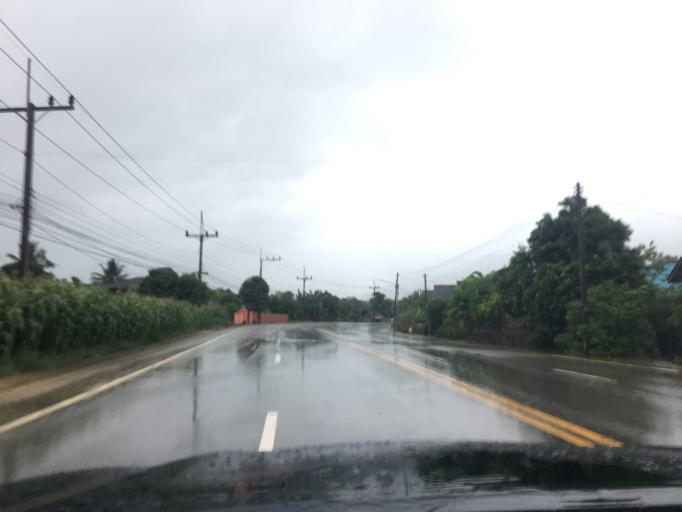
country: TH
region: Chiang Rai
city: Chiang Saen
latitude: 20.3007
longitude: 100.2460
